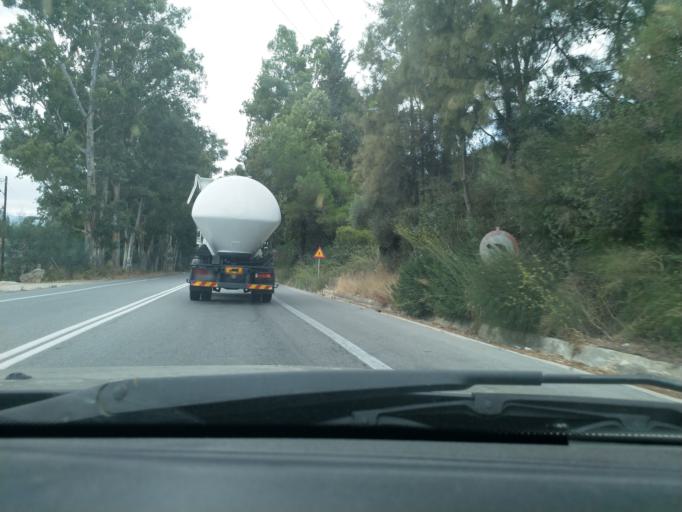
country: GR
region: Crete
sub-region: Nomos Chanias
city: Georgioupolis
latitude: 35.3791
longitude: 24.2036
